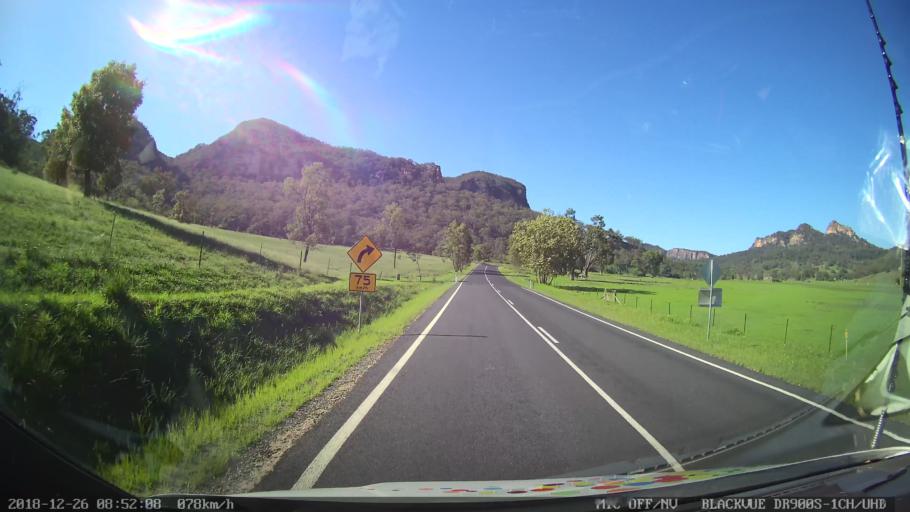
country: AU
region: New South Wales
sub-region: Mid-Western Regional
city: Kandos
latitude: -32.5934
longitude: 150.0874
